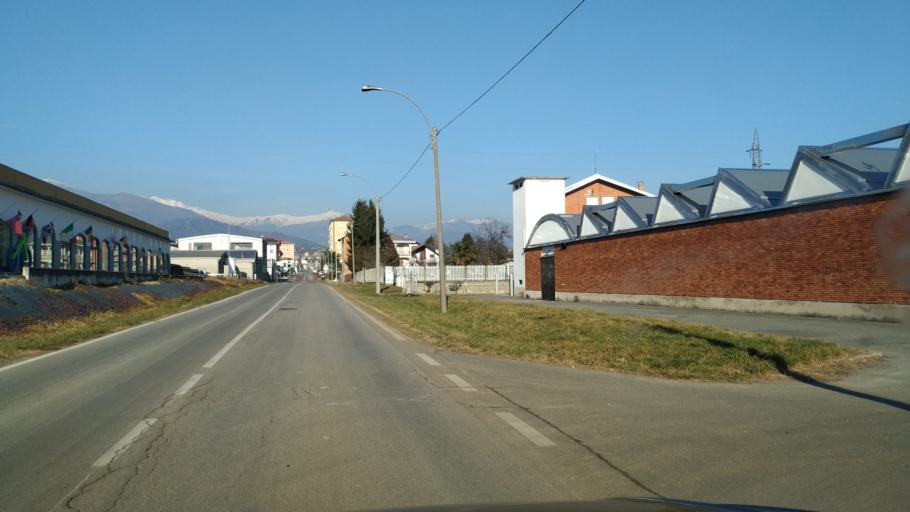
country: IT
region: Piedmont
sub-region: Provincia di Biella
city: Camburzano
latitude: 45.5388
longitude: 8.0123
